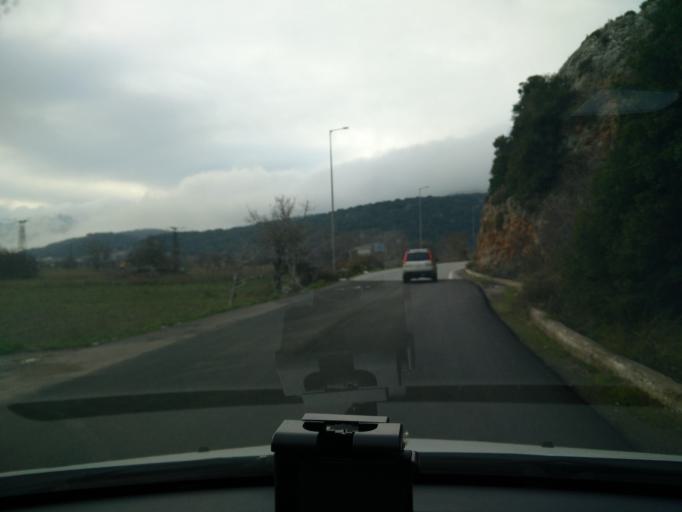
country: GR
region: Crete
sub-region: Nomos Irakleiou
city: Malia
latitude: 35.2018
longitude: 25.4810
